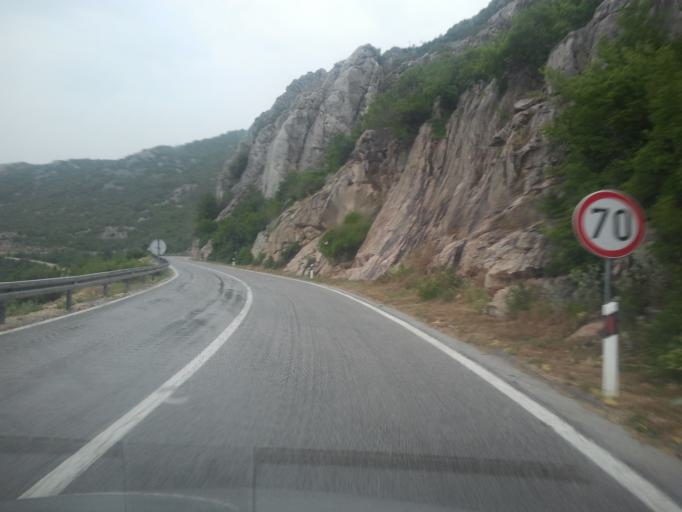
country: HR
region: Zadarska
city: Gracac
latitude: 44.2314
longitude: 15.8027
